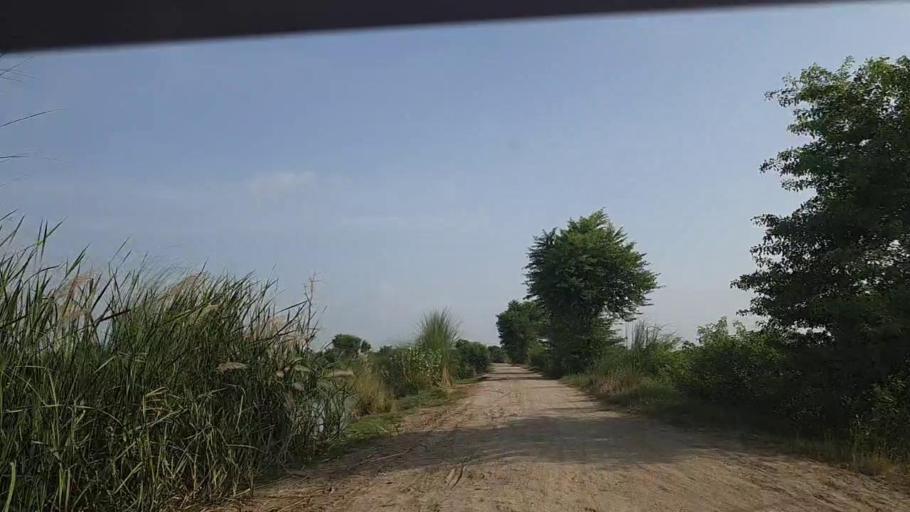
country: PK
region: Sindh
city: Ghotki
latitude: 27.9992
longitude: 69.2618
